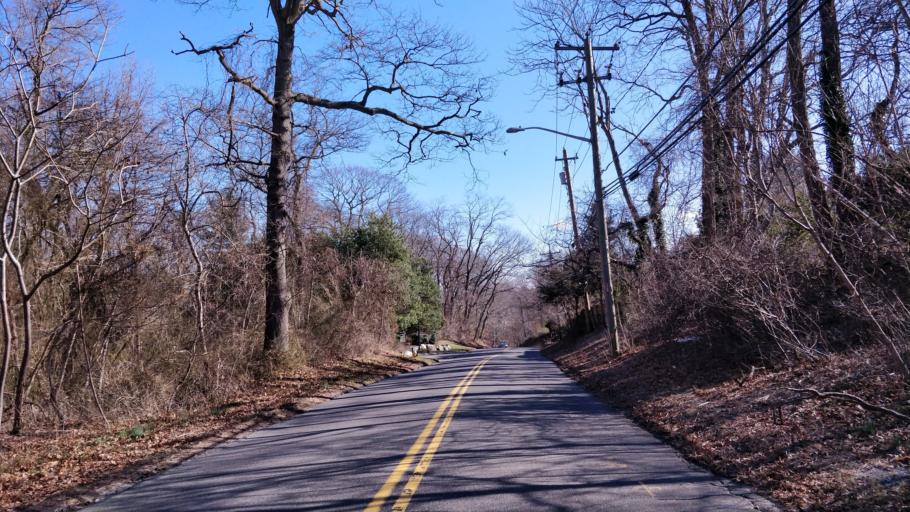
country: US
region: New York
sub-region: Suffolk County
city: Mount Sinai
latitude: 40.9482
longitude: -73.0483
